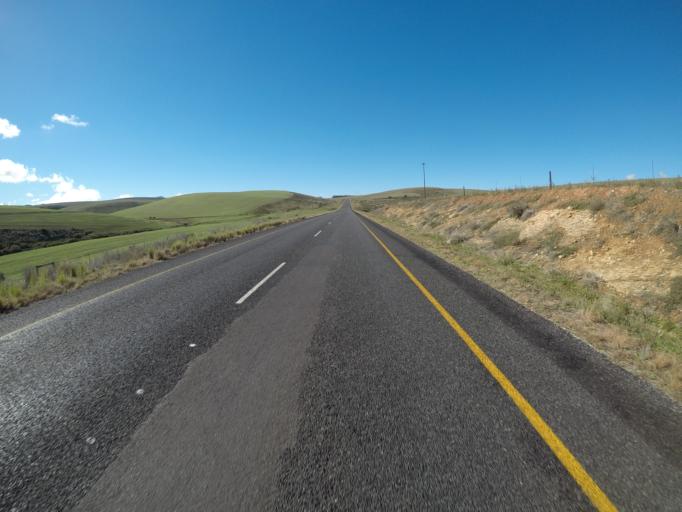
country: ZA
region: Western Cape
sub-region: Overberg District Municipality
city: Caledon
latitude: -34.1492
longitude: 19.4832
